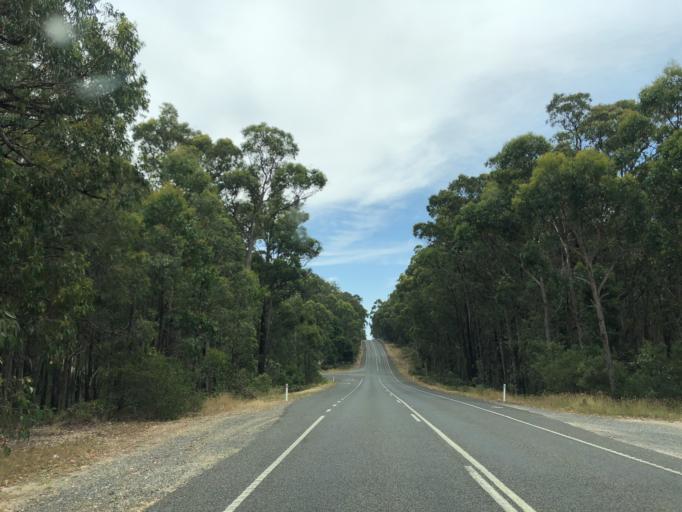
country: AU
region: Victoria
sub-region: Moorabool
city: Bacchus Marsh
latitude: -37.4946
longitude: 144.3085
